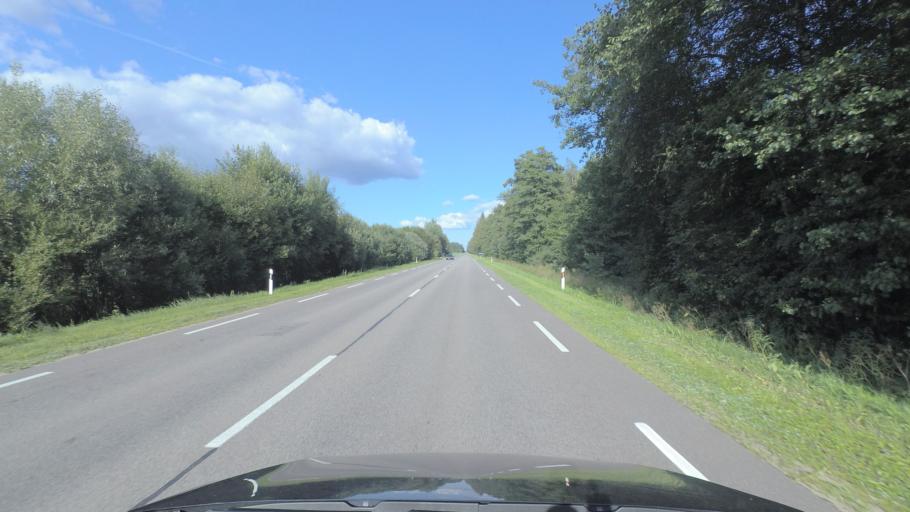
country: LT
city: Pabrade
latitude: 54.9595
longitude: 25.6914
